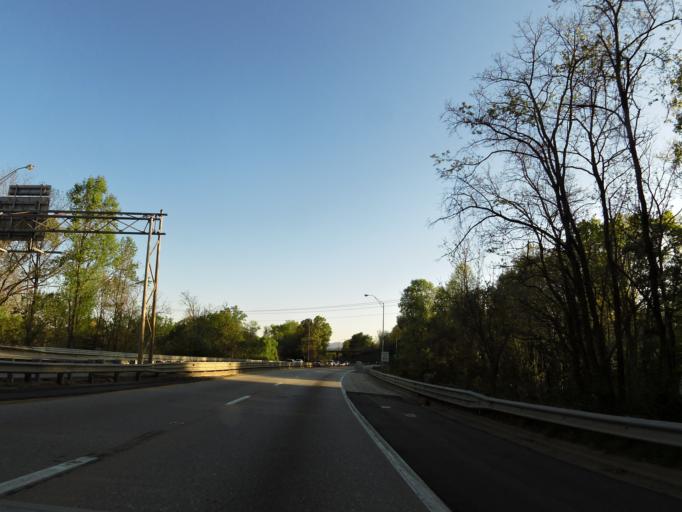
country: US
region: North Carolina
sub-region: Buncombe County
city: Asheville
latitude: 35.5741
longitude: -82.5835
